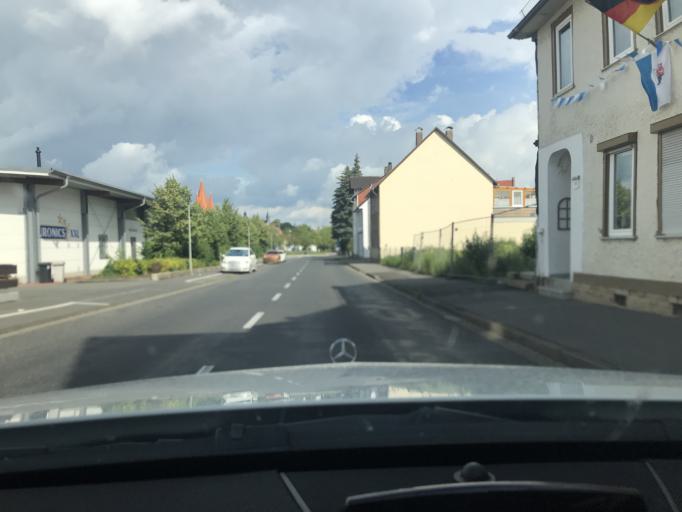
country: DE
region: Hesse
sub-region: Regierungsbezirk Kassel
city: Eschwege
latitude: 51.1843
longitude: 10.0652
